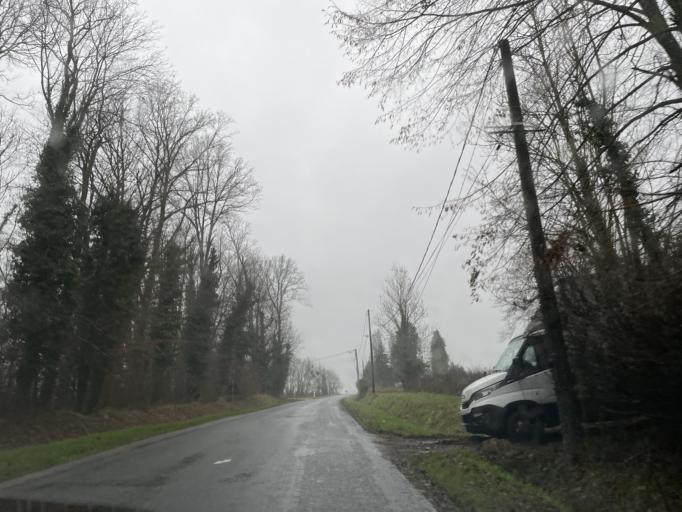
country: FR
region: Ile-de-France
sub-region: Departement de Seine-et-Marne
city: Pommeuse
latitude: 48.8216
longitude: 3.0091
